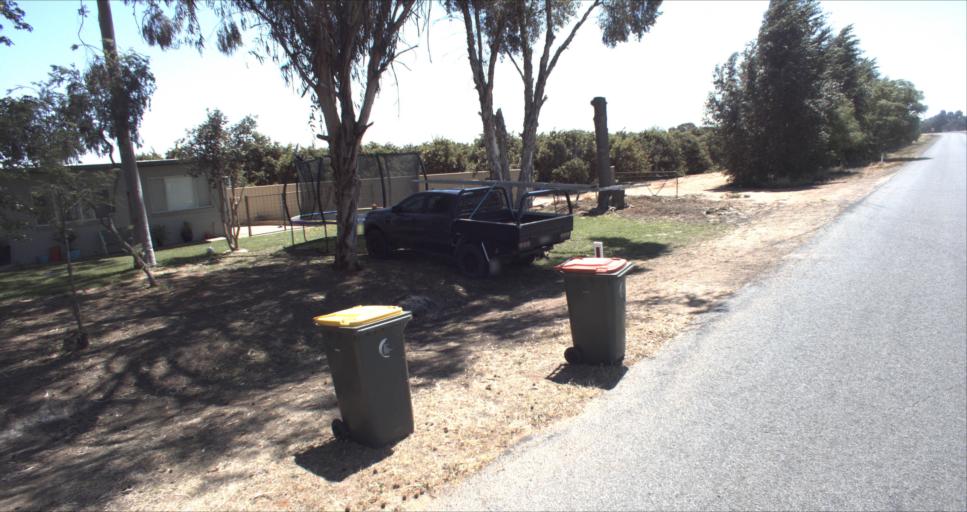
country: AU
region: New South Wales
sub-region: Leeton
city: Leeton
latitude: -34.5421
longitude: 146.3945
